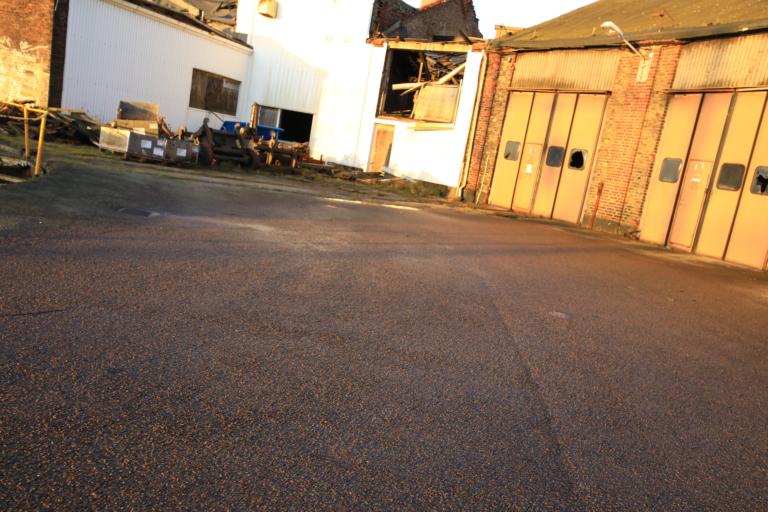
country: SE
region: Halland
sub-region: Varbergs Kommun
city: Varberg
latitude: 57.1139
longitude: 12.2501
